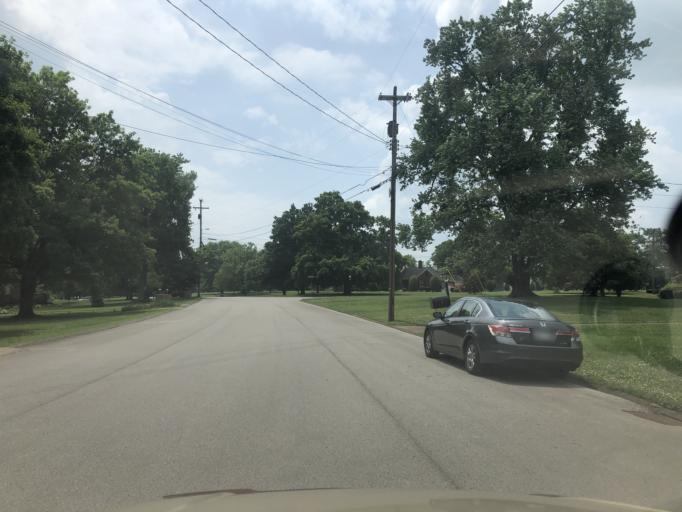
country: US
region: Tennessee
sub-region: Davidson County
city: Lakewood
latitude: 36.2417
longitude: -86.6218
